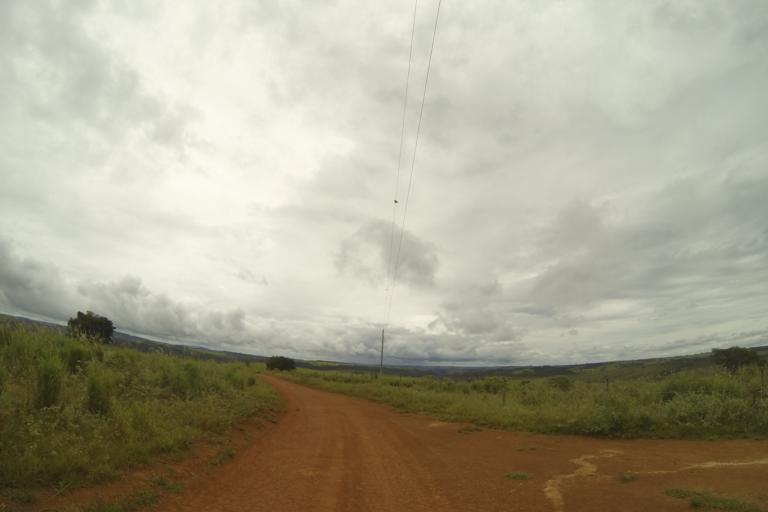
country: BR
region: Minas Gerais
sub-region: Ibia
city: Ibia
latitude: -19.7478
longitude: -46.5289
